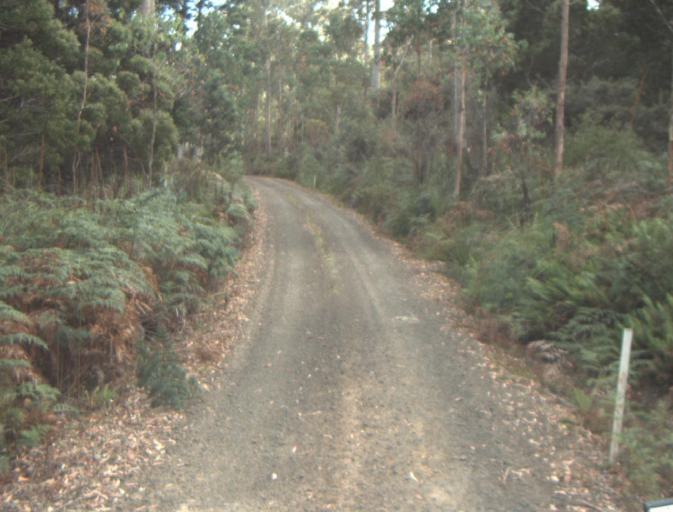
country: AU
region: Tasmania
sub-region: Launceston
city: Mayfield
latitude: -41.2921
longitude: 147.2400
